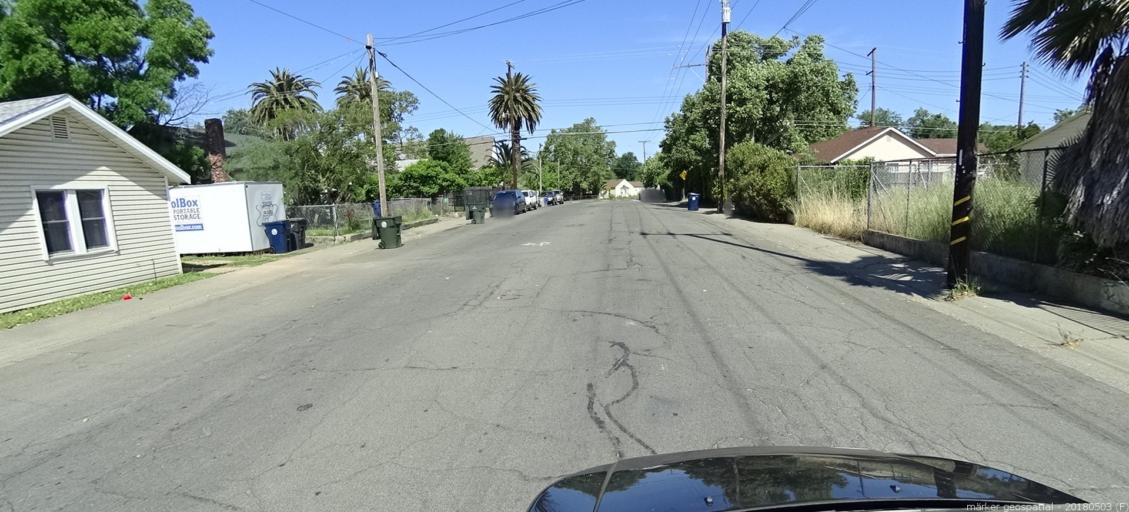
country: US
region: California
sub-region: Sacramento County
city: Arden-Arcade
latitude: 38.6177
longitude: -121.4407
